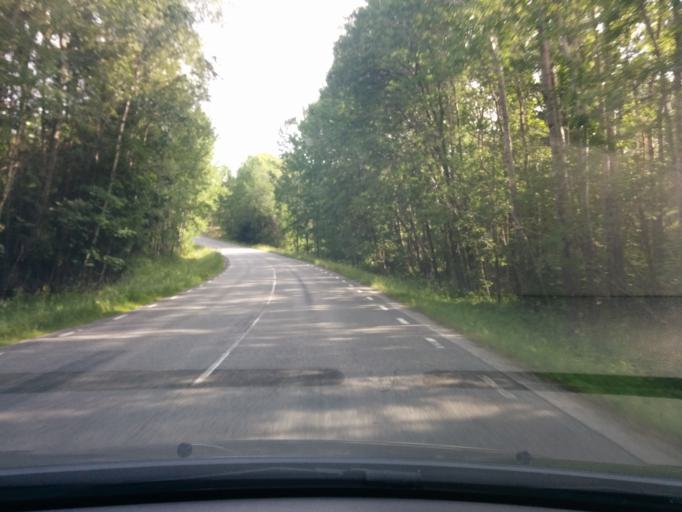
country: SE
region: Stockholm
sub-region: Varmdo Kommun
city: Holo
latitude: 59.3324
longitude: 18.7190
